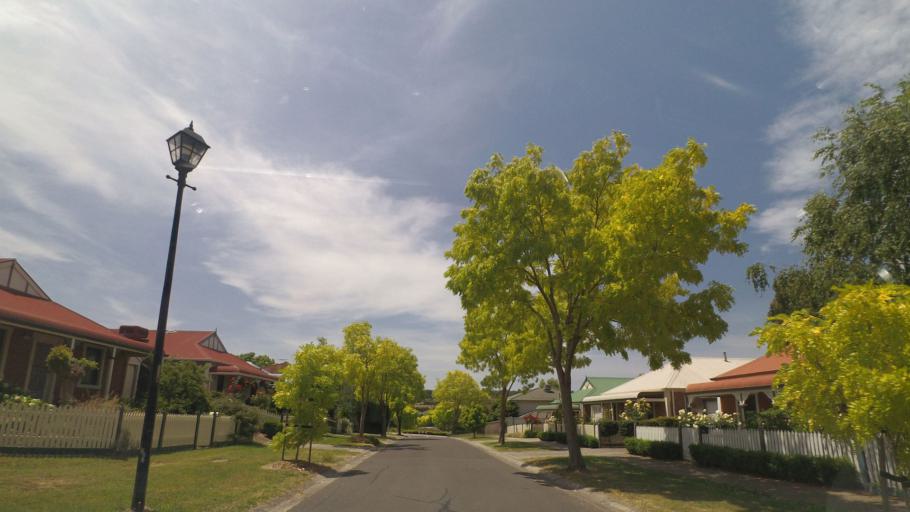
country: AU
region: Victoria
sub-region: Maroondah
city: Croydon North
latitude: -37.7596
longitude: 145.2982
